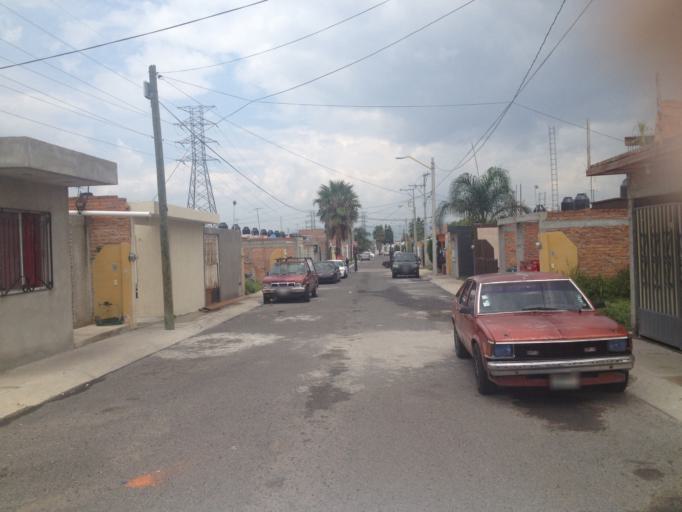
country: MX
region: Aguascalientes
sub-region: Aguascalientes
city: San Sebastian [Fraccionamiento]
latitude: 21.8178
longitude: -102.2666
